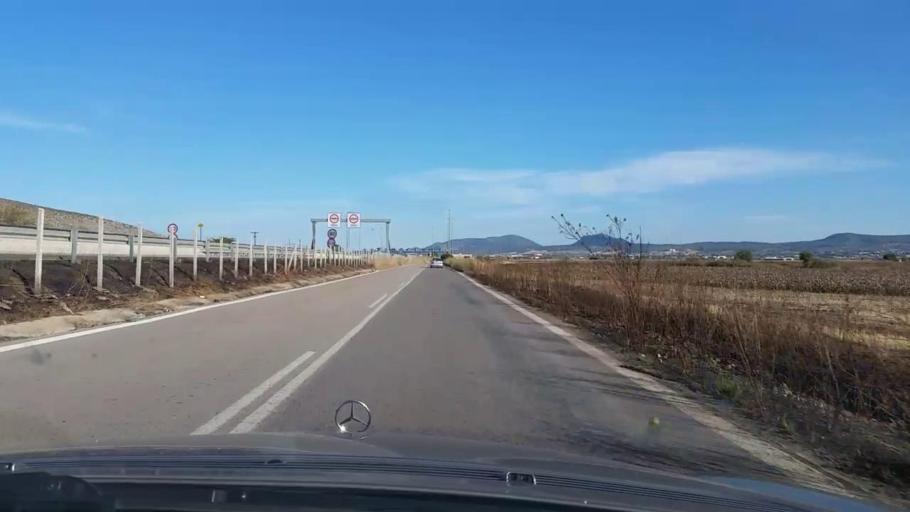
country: GR
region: Central Greece
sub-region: Nomos Voiotias
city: Thivai
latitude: 38.3722
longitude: 23.2805
